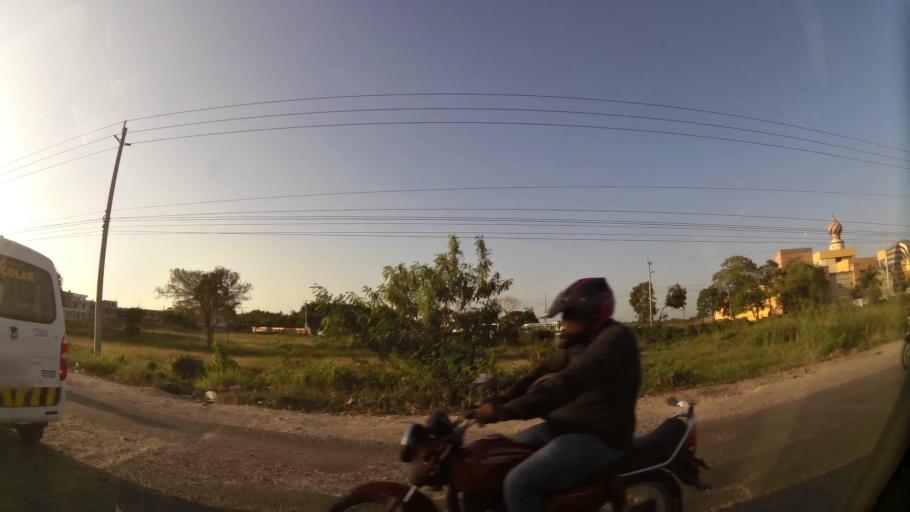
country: CO
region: Bolivar
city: Cartagena
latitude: 10.3995
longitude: -75.4684
